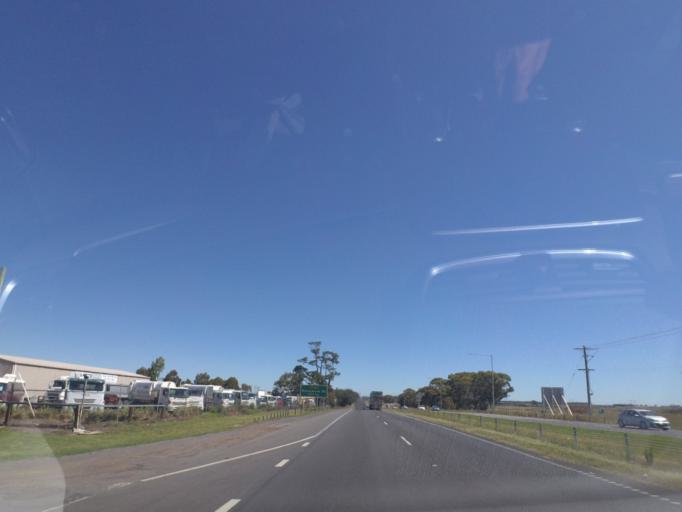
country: AU
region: Victoria
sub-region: Hume
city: Craigieburn
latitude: -37.5306
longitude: 144.9473
